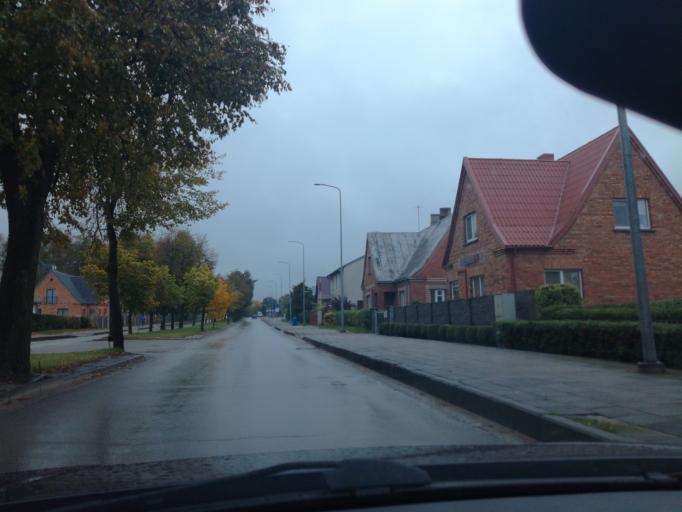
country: LT
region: Alytaus apskritis
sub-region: Alytus
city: Alytus
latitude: 54.4030
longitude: 24.0610
